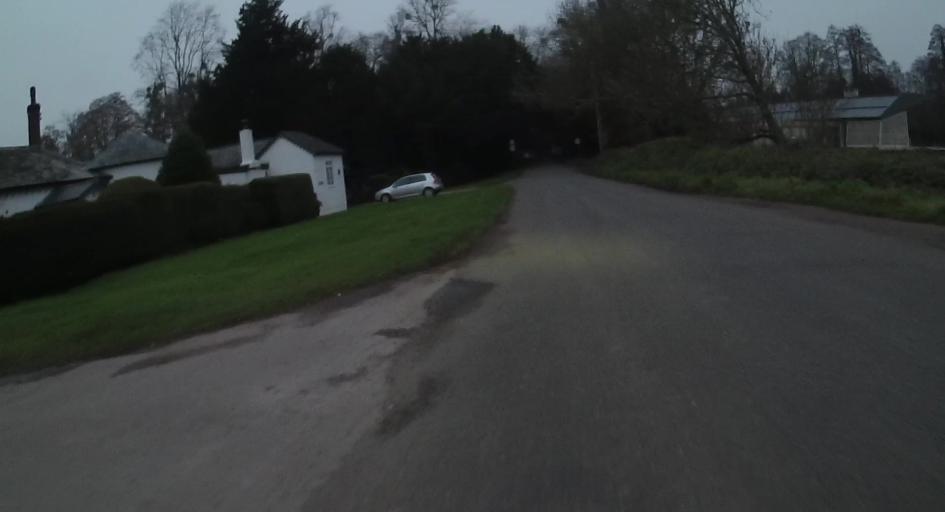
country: GB
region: England
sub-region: Hampshire
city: Kings Worthy
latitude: 51.0888
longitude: -1.2354
